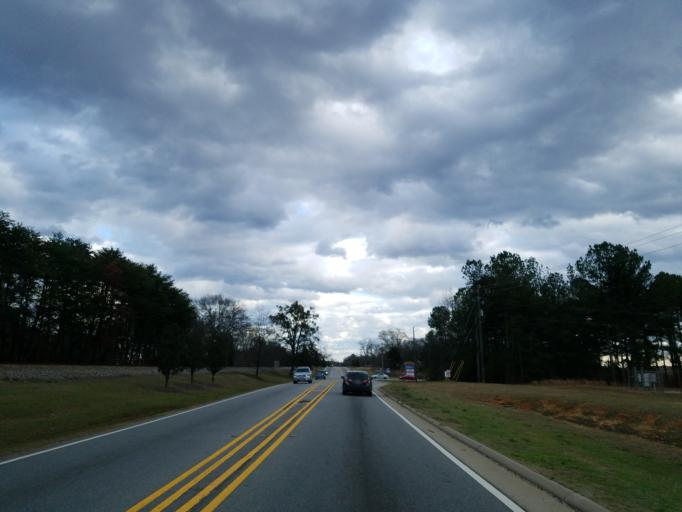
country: US
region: Georgia
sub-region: Henry County
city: Locust Grove
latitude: 33.3612
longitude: -84.1203
